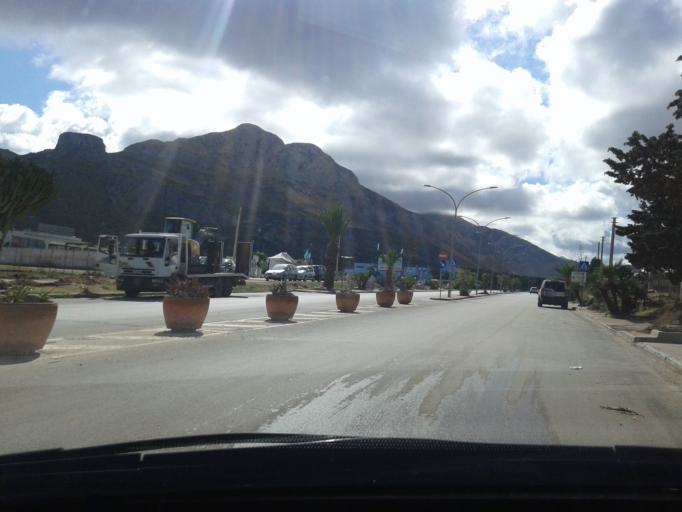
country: IT
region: Sicily
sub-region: Trapani
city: San Vito Lo Capo
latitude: 38.1672
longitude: 12.7351
